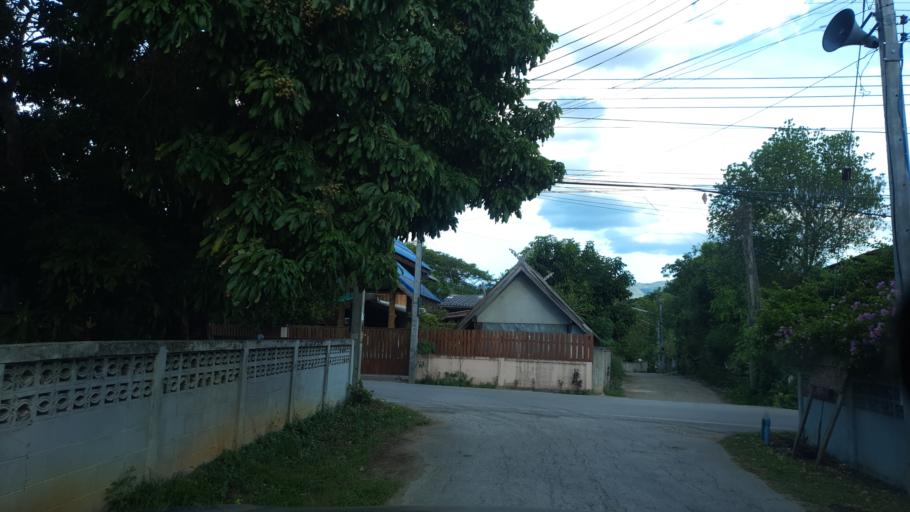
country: TH
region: Lampang
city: Sop Prap
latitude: 17.8703
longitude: 99.3077
